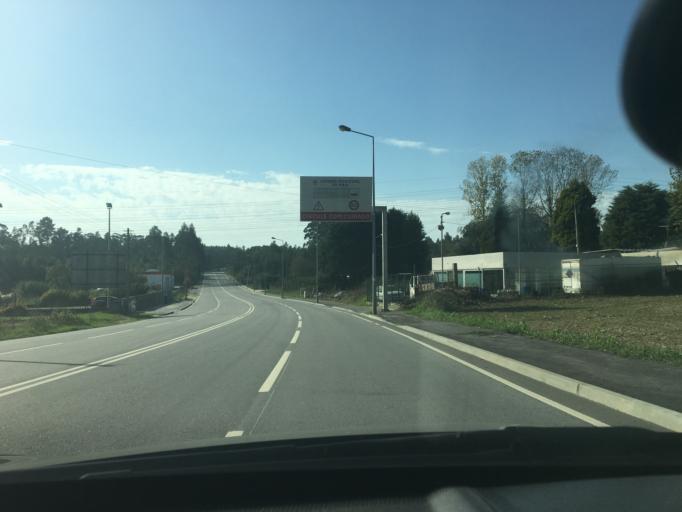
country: PT
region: Porto
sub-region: Maia
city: Anta
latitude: 41.2593
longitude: -8.6226
